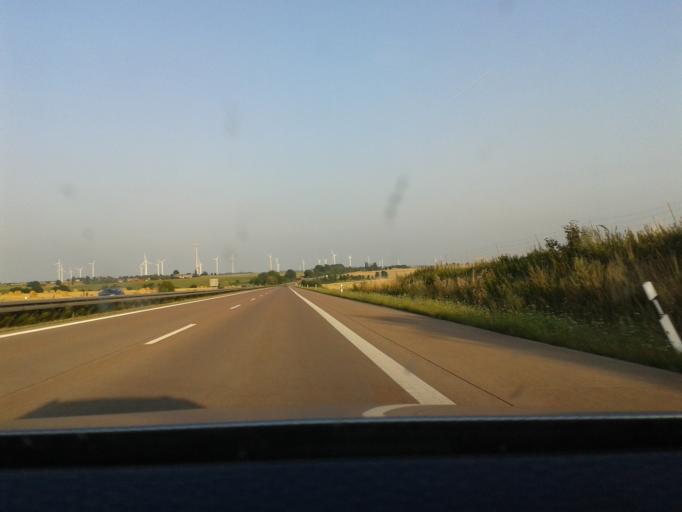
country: DE
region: Saxony
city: Mutzschen
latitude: 51.2378
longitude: 12.8736
